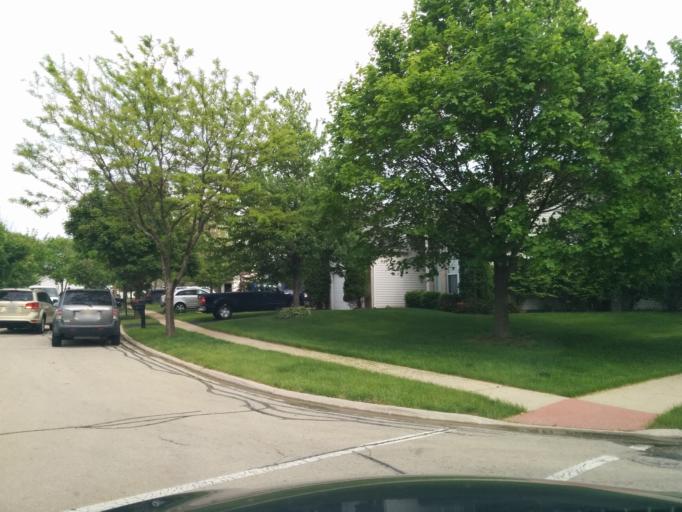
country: US
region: Illinois
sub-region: Will County
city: Crystal Lawns
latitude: 41.6187
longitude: -88.1488
